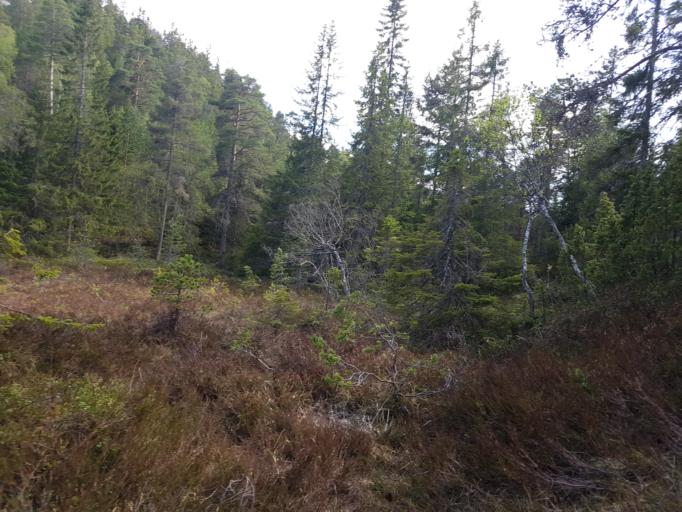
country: NO
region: Sor-Trondelag
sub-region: Trondheim
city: Trondheim
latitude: 63.4372
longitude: 10.2968
